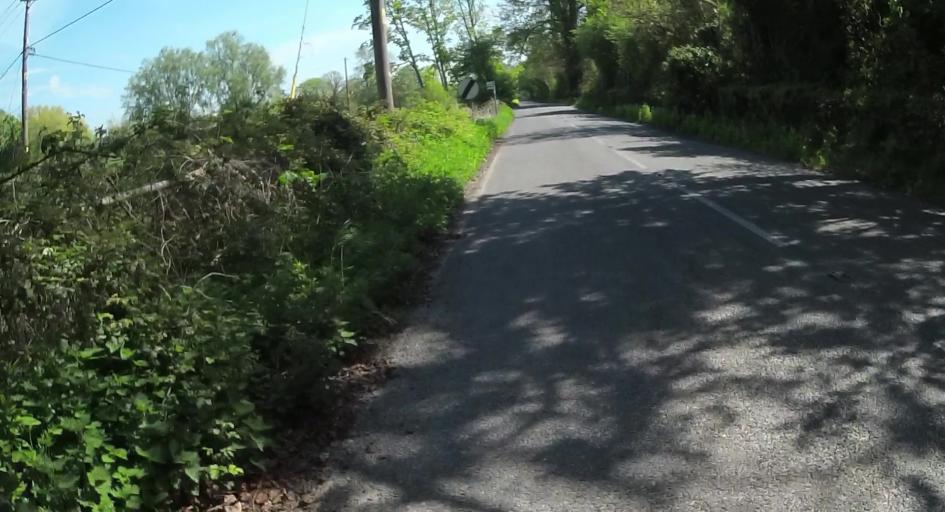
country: GB
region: England
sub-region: Hampshire
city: Andover
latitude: 51.1692
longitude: -1.4388
